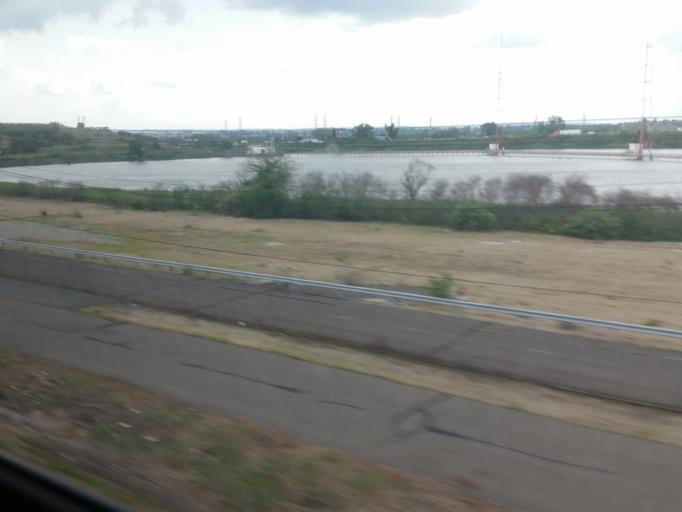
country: US
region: New Jersey
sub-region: Hudson County
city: Jersey City
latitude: 40.7514
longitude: -74.1017
